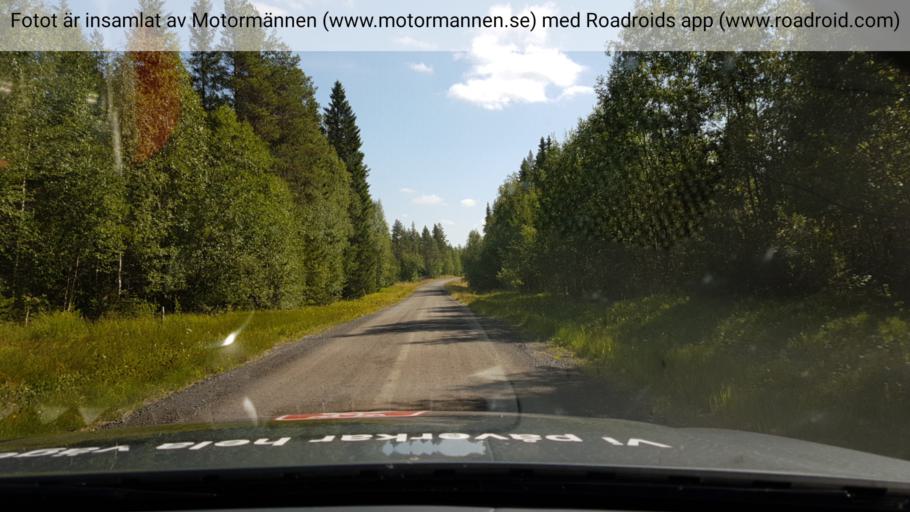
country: SE
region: Jaemtland
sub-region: Stroemsunds Kommun
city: Stroemsund
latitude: 63.3451
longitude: 15.3817
